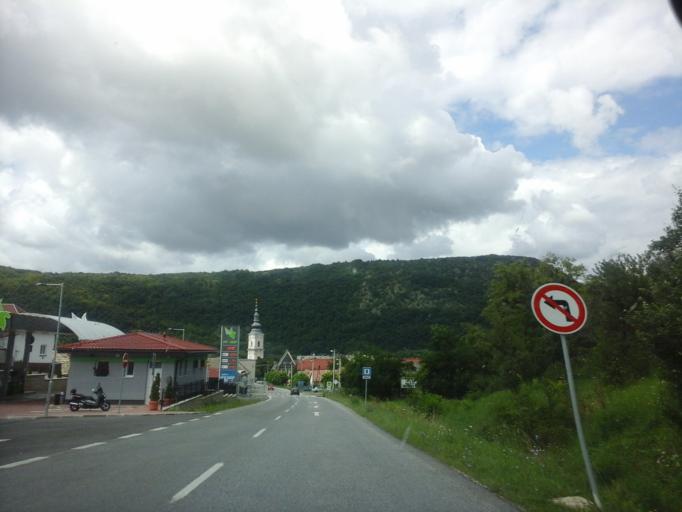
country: SK
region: Kosicky
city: Roznava
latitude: 48.5434
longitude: 20.4064
